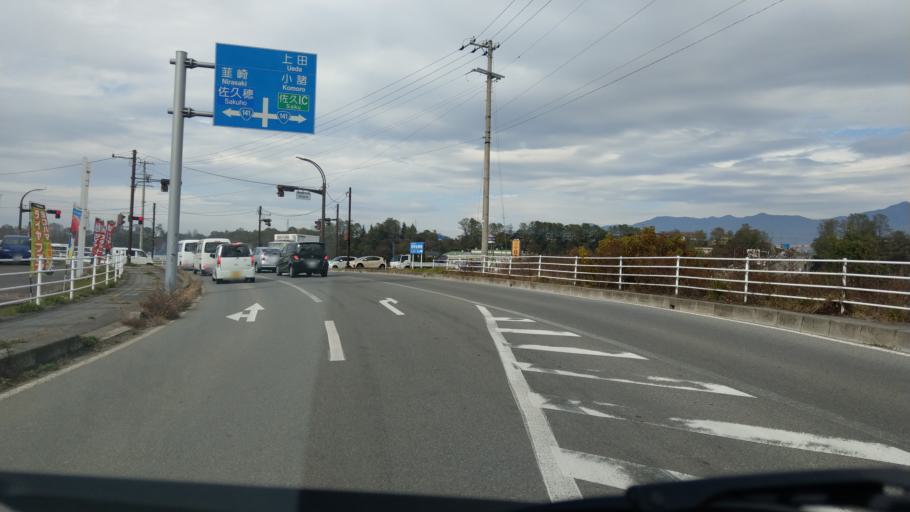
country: JP
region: Nagano
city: Saku
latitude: 36.2432
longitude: 138.4677
